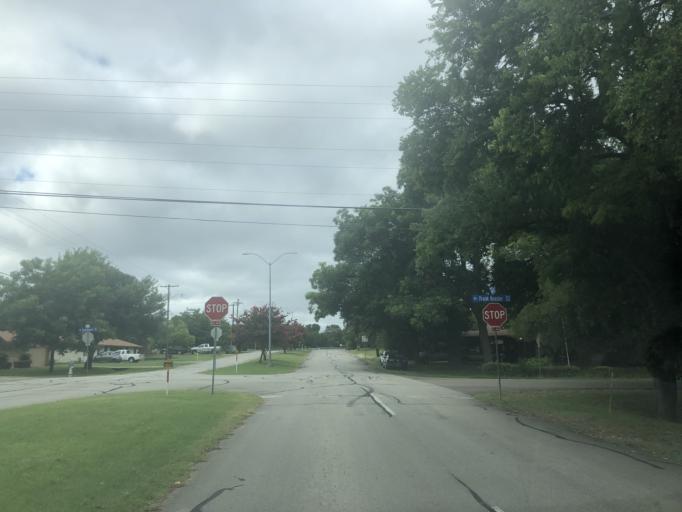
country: US
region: Texas
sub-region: Dallas County
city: Duncanville
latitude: 32.6687
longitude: -96.9157
